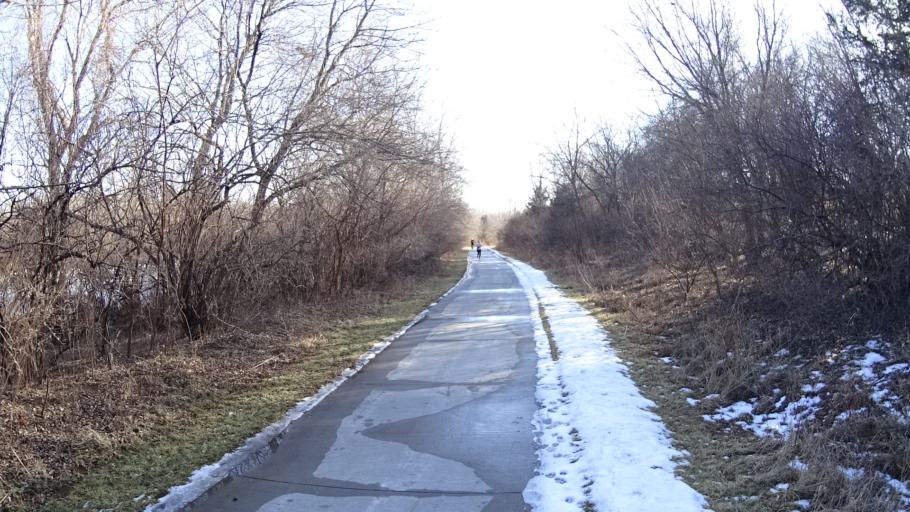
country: US
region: Nebraska
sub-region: Douglas County
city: Bennington
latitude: 41.3119
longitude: -96.1270
